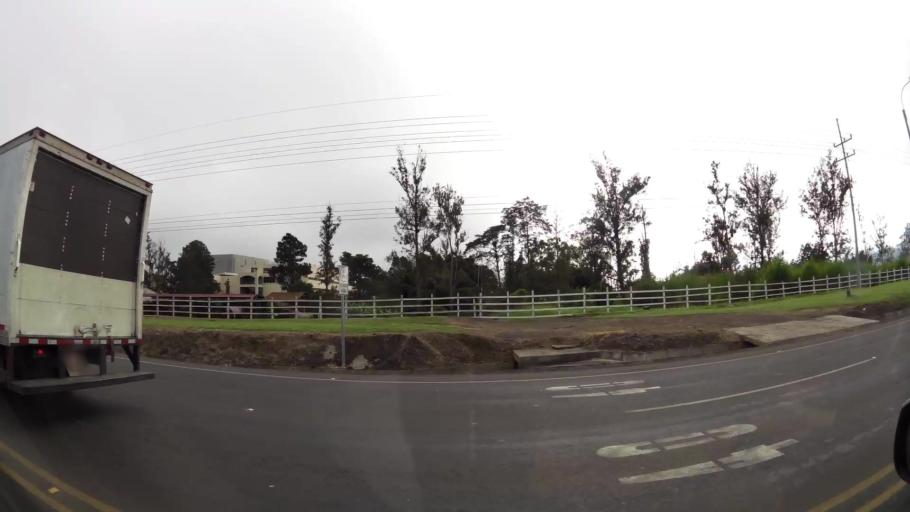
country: CR
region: Cartago
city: Cartago
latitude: 9.8657
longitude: -83.9453
